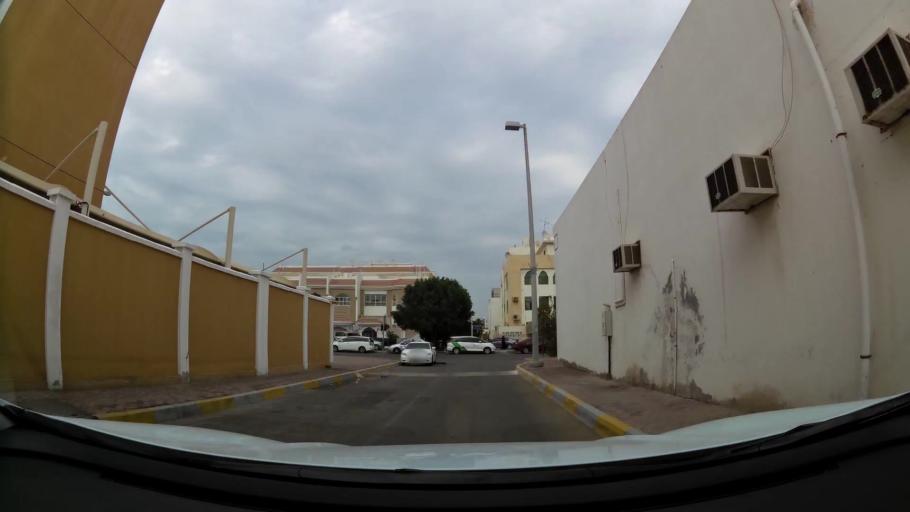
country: AE
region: Abu Dhabi
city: Abu Dhabi
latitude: 24.4422
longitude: 54.4006
